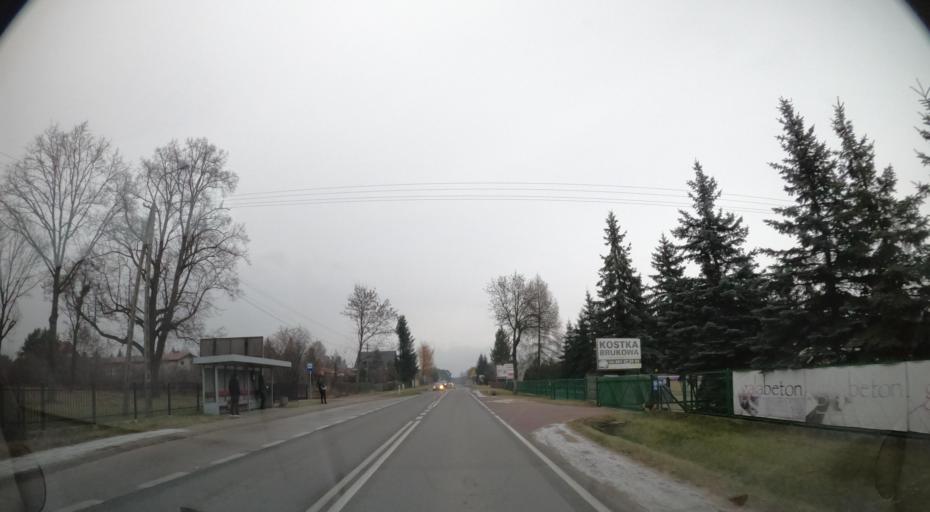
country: PL
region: Masovian Voivodeship
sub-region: Powiat radomski
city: Jastrzebia
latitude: 51.4276
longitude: 21.2305
